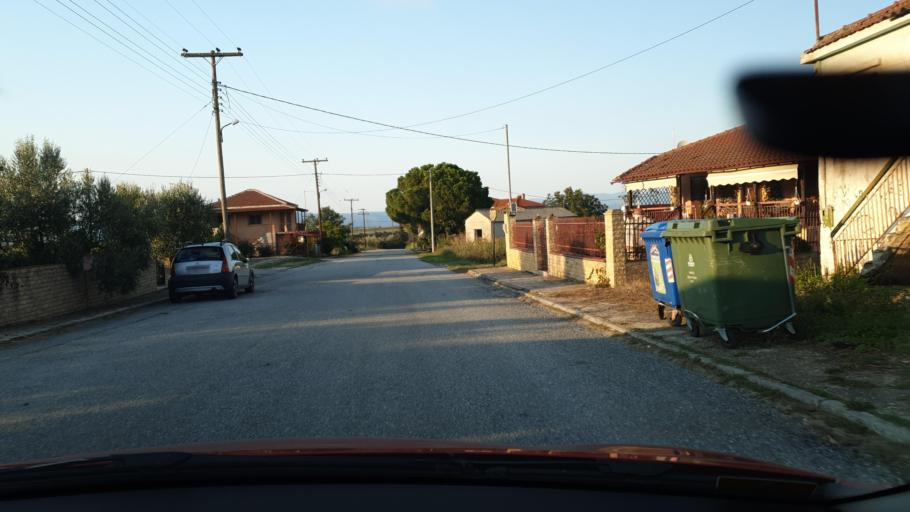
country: GR
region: Central Macedonia
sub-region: Nomos Thessalonikis
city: Nea Apollonia
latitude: 40.5478
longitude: 23.4488
